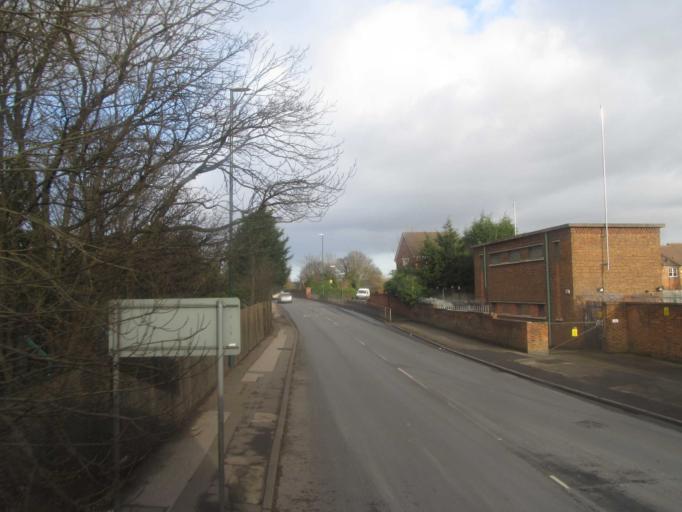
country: GB
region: England
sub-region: Nottinghamshire
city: Hucknall
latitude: 52.9881
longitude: -1.2025
